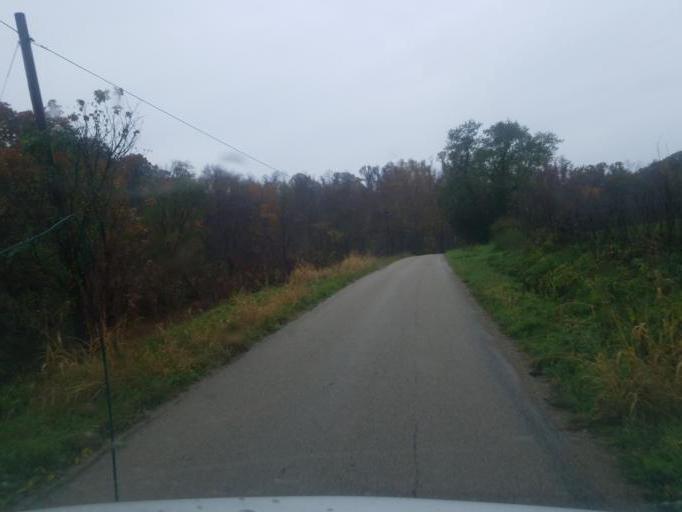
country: US
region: Ohio
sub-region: Washington County
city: Beverly
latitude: 39.4780
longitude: -81.7355
